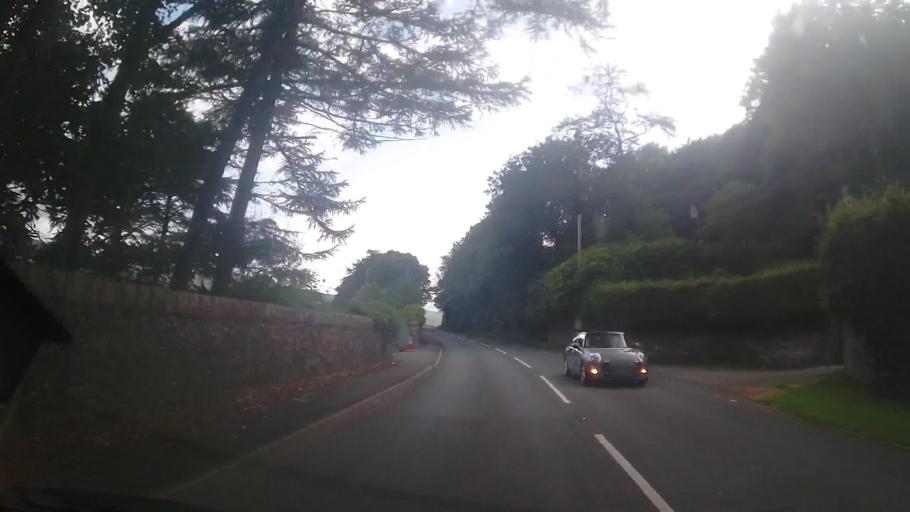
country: GB
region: Wales
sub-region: Gwynedd
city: Barmouth
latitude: 52.7274
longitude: -4.0313
